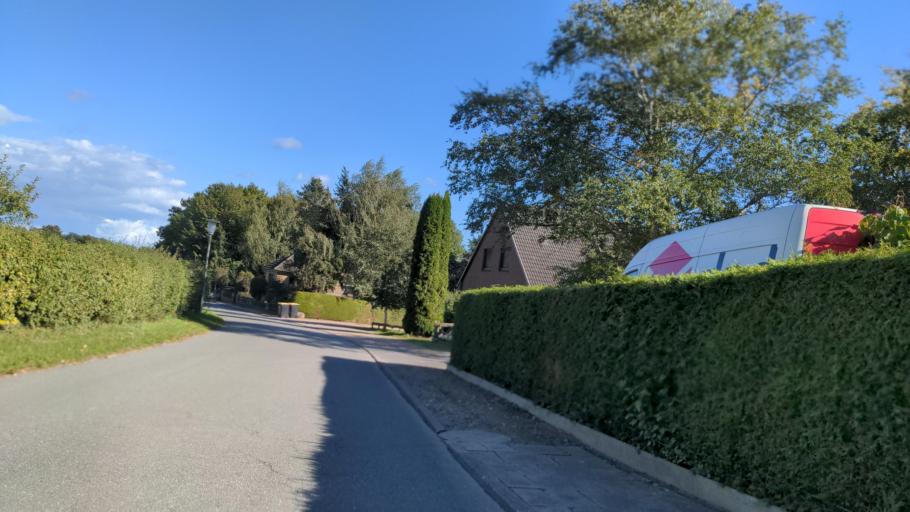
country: DE
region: Schleswig-Holstein
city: Gromitz
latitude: 54.1727
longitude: 10.9396
